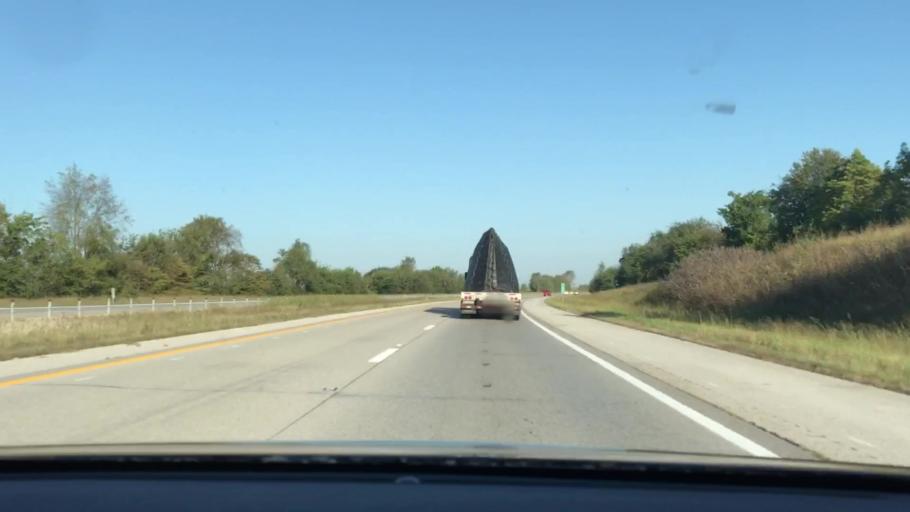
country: US
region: Kentucky
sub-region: Trigg County
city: Cadiz
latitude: 36.8550
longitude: -87.7016
